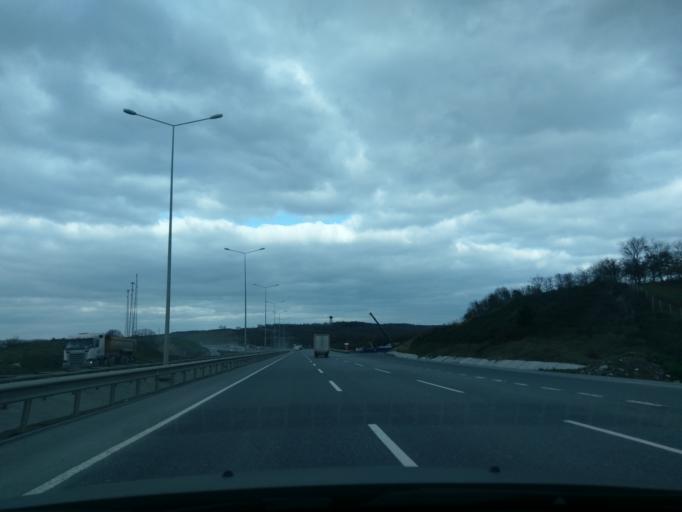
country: TR
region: Istanbul
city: Kemerburgaz
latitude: 41.2238
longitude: 28.8342
